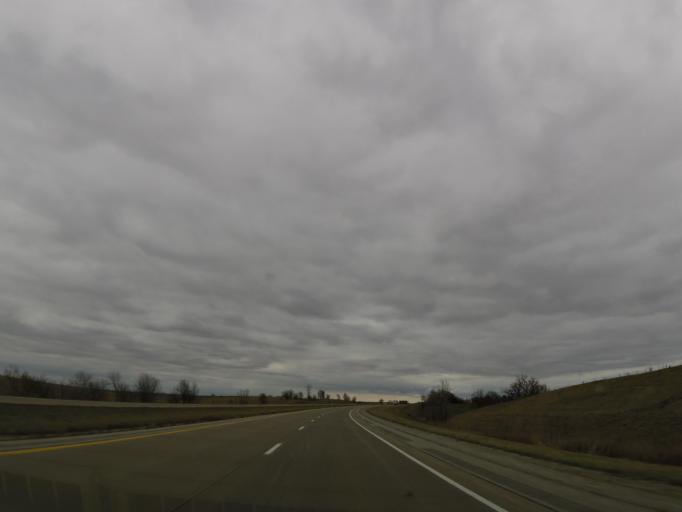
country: US
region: Iowa
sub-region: Washington County
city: Washington
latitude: 41.3058
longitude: -91.5393
